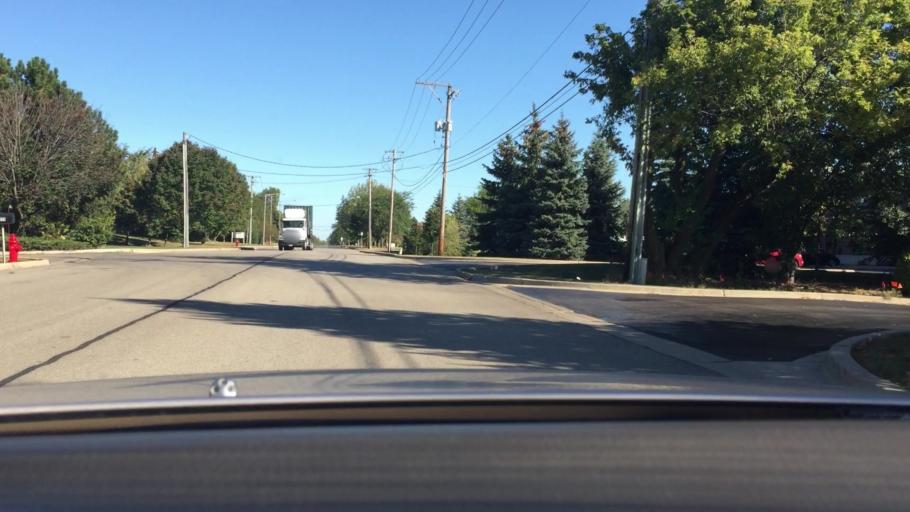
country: US
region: Illinois
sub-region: Lake County
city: Forest Lake
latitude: 42.2000
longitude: -88.0676
